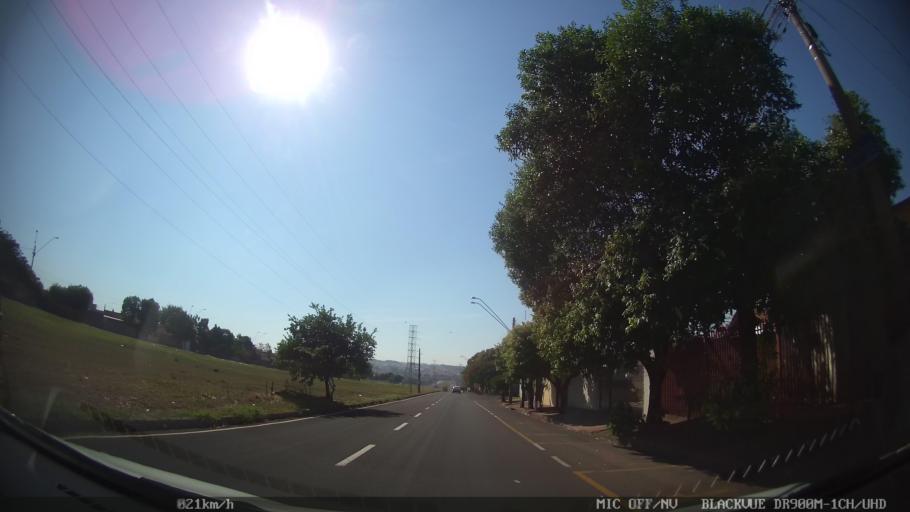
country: BR
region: Sao Paulo
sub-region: Sao Jose Do Rio Preto
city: Sao Jose do Rio Preto
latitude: -20.7653
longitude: -49.3803
